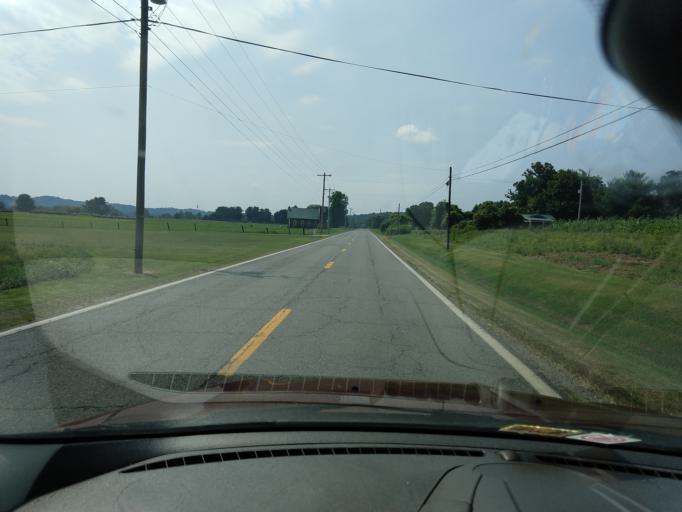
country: US
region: West Virginia
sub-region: Mason County
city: New Haven
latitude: 38.9467
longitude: -81.9203
